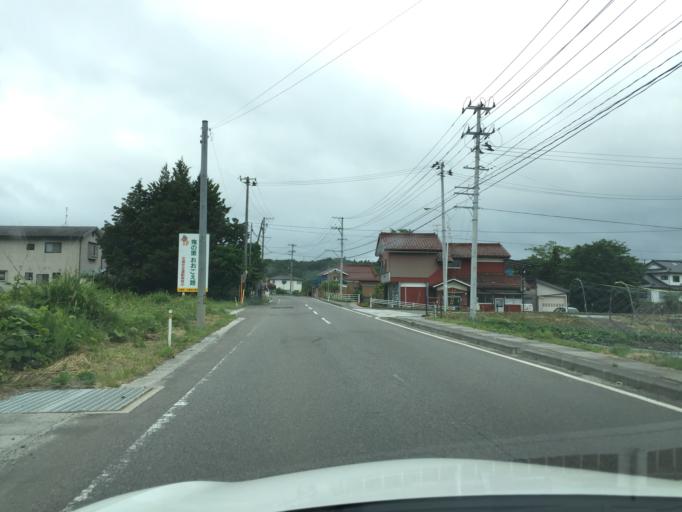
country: JP
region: Fukushima
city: Funehikimachi-funehiki
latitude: 37.4130
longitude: 140.6096
